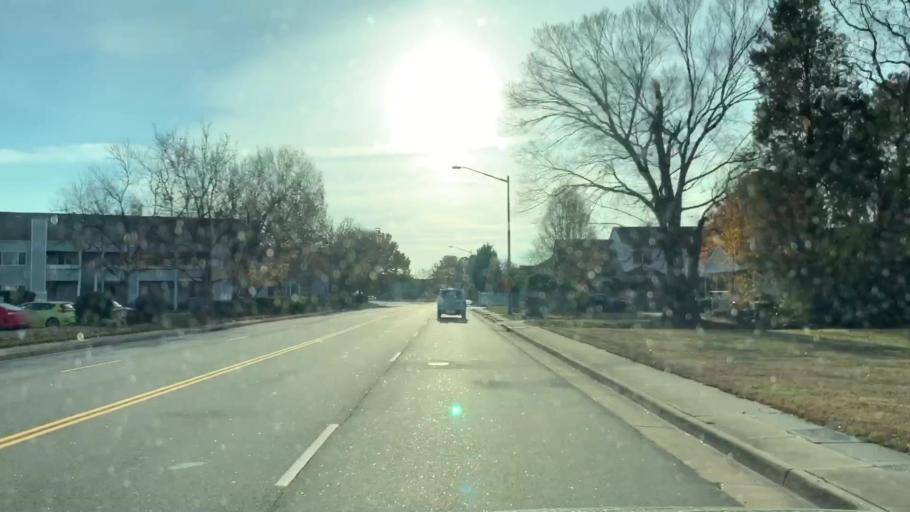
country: US
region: Virginia
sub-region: City of Chesapeake
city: Chesapeake
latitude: 36.7906
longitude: -76.1659
